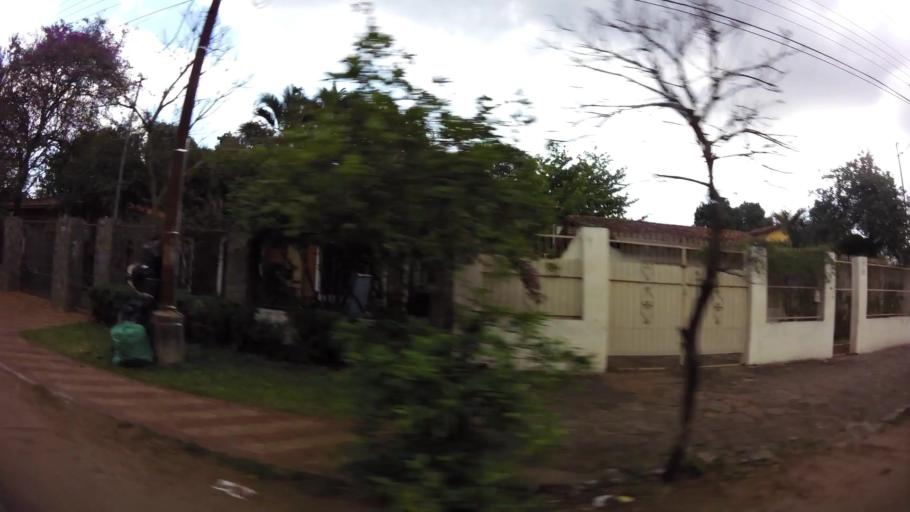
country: PY
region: Central
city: Fernando de la Mora
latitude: -25.3372
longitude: -57.5538
